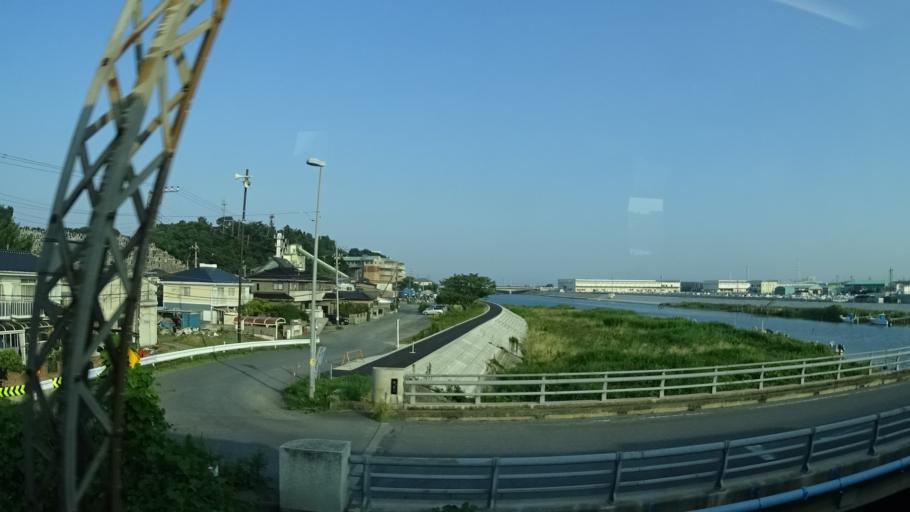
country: JP
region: Ibaraki
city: Funaishikawa
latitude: 36.4923
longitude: 140.6072
